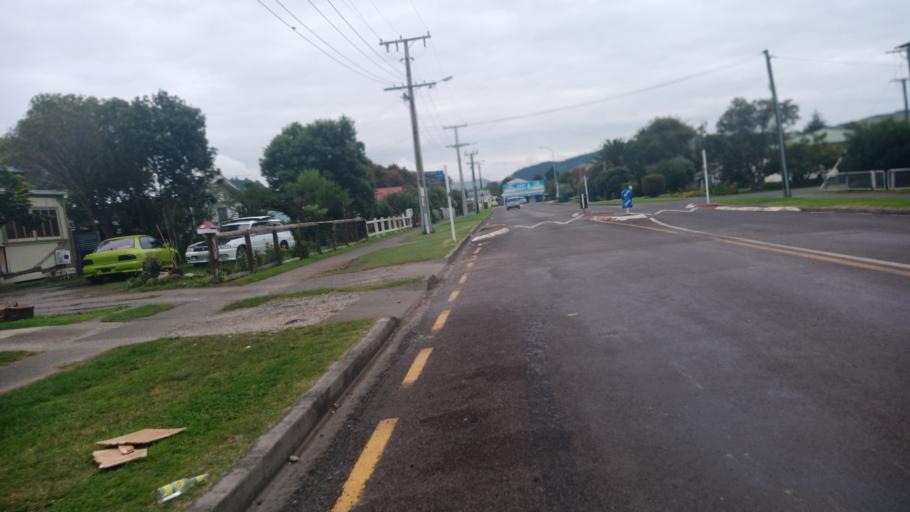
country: NZ
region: Gisborne
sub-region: Gisborne District
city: Gisborne
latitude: -38.6761
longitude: 178.0426
